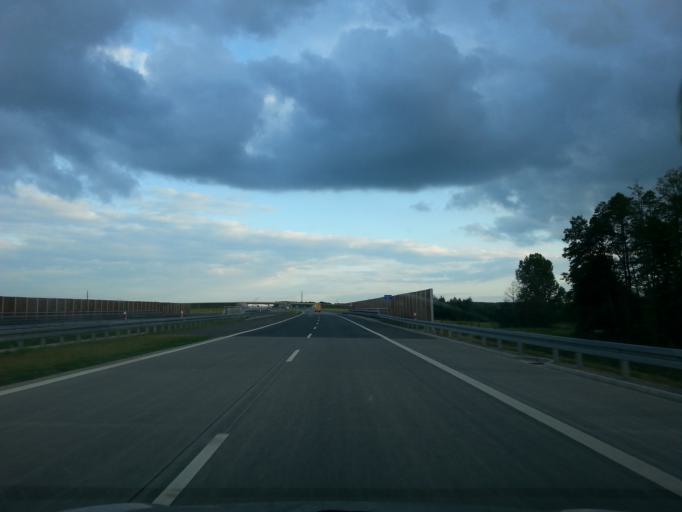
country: PL
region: Lodz Voivodeship
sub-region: Powiat sieradzki
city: Sieradz
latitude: 51.5389
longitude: 18.6974
